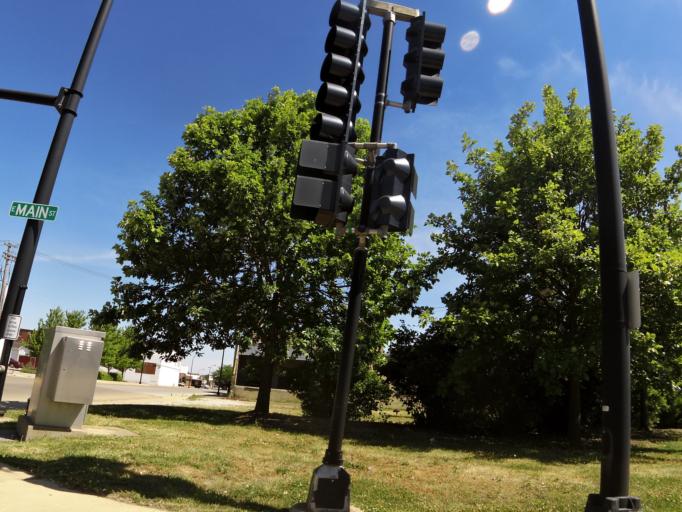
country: US
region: Illinois
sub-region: Vermilion County
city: Danville
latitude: 40.1247
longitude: -87.6269
